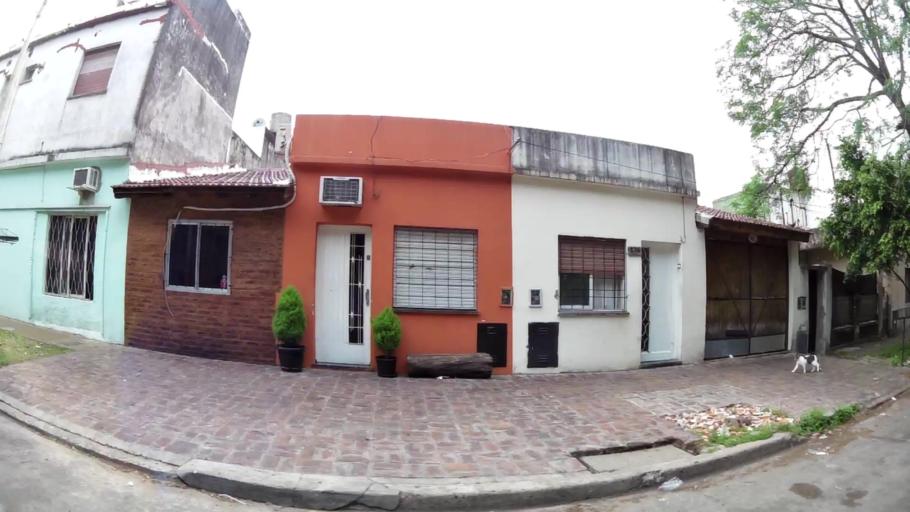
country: AR
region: Buenos Aires
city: San Justo
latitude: -34.6917
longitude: -58.5177
